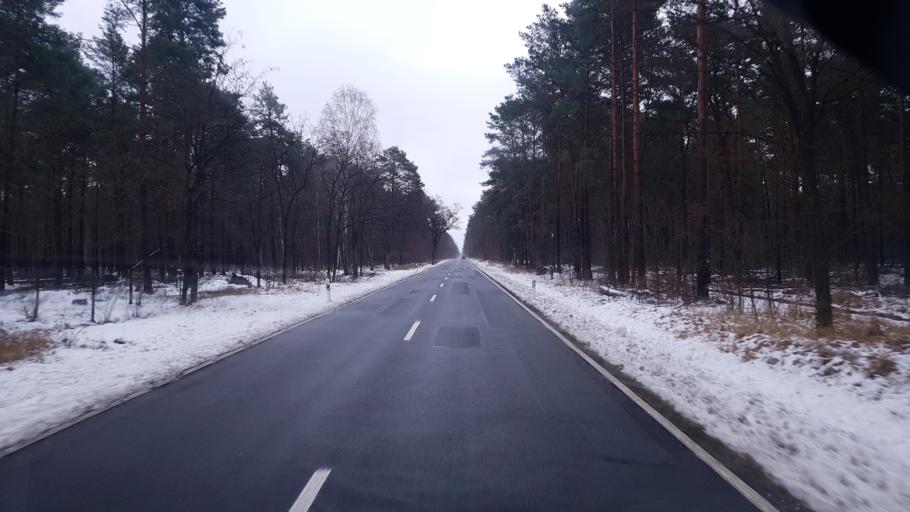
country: DE
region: Brandenburg
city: Jamlitz
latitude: 51.9825
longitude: 14.4460
